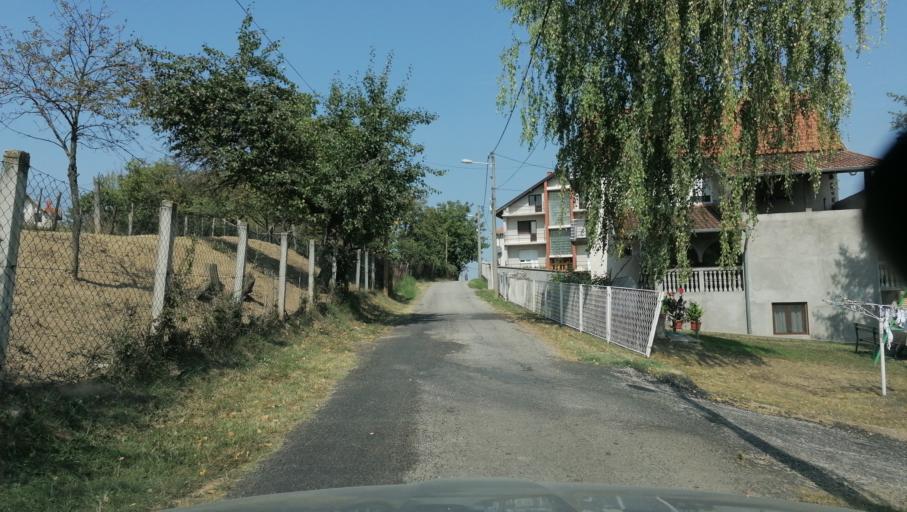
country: RS
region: Central Serbia
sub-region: Belgrade
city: Zvezdara
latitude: 44.6931
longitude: 20.5568
